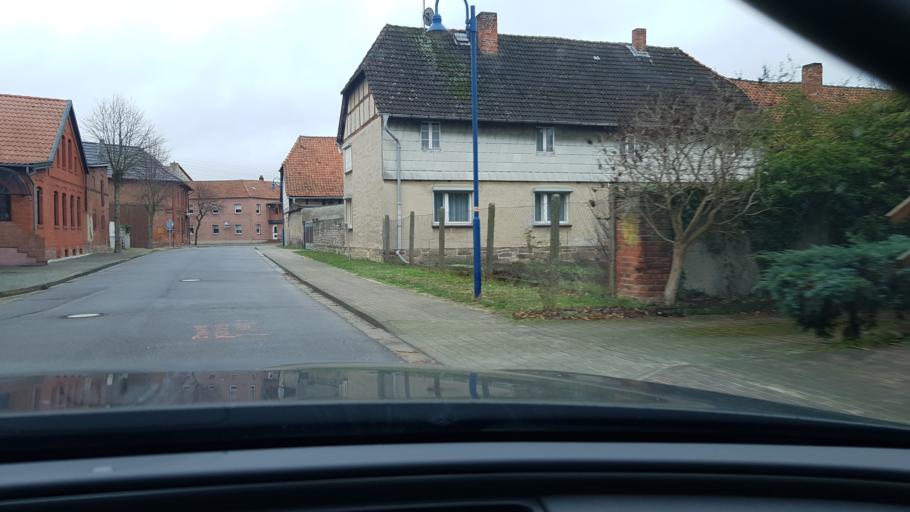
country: DE
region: Saxony-Anhalt
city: Weferlingen
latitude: 52.4025
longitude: 11.1149
